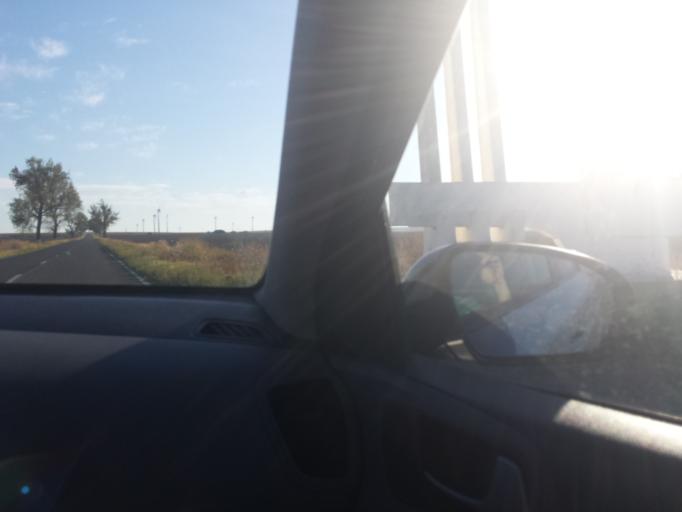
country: RO
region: Constanta
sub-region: Comuna Saraiu
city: Saraiu
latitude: 44.7529
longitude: 28.1927
